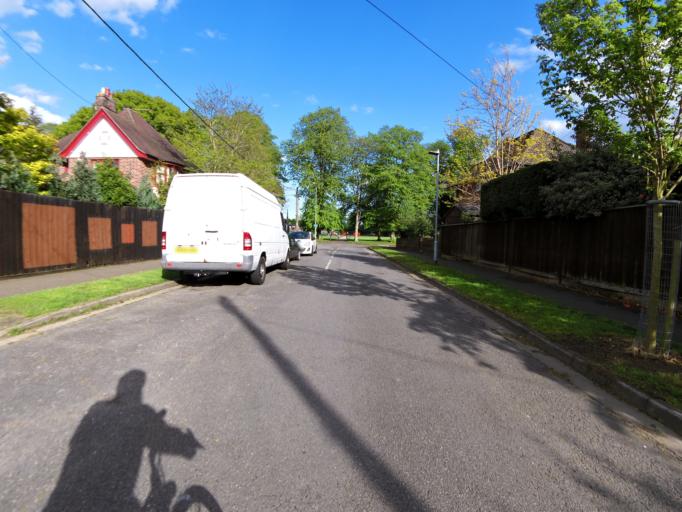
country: GB
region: England
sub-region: Suffolk
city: Stowmarket
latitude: 52.1896
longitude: 0.9864
